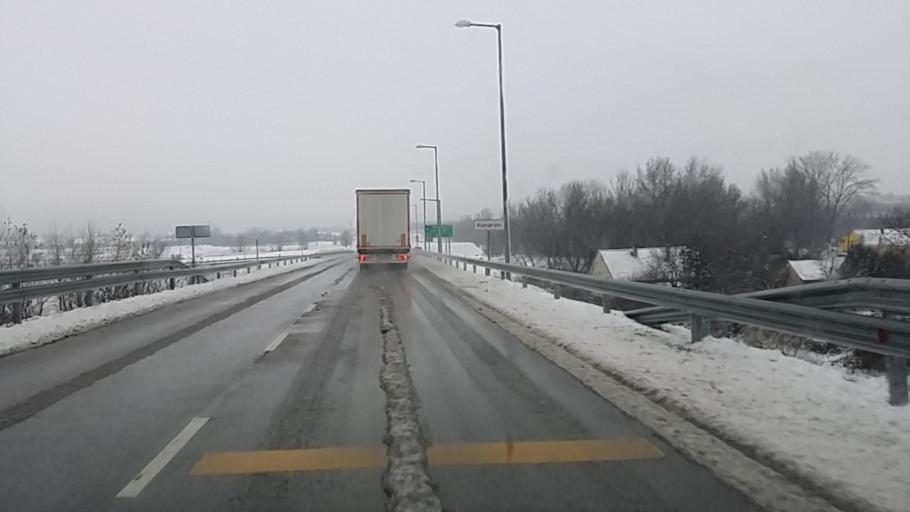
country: HU
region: Komarom-Esztergom
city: Komarom
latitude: 47.7437
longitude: 18.0908
